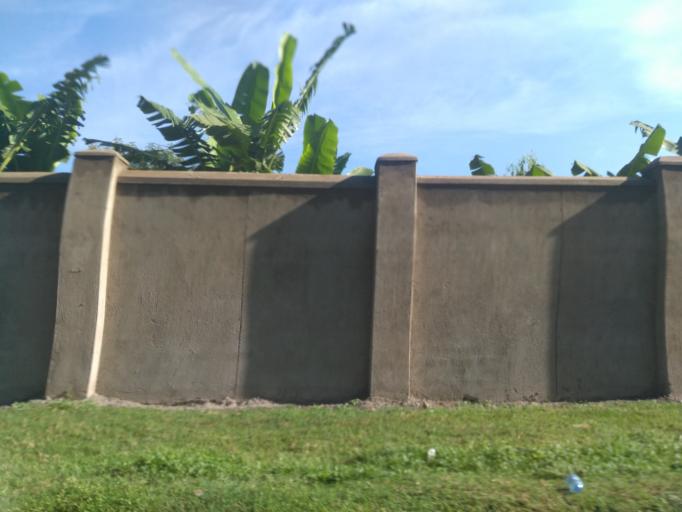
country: UG
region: Eastern Region
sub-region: Jinja District
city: Jinja
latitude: 0.4451
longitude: 33.1926
